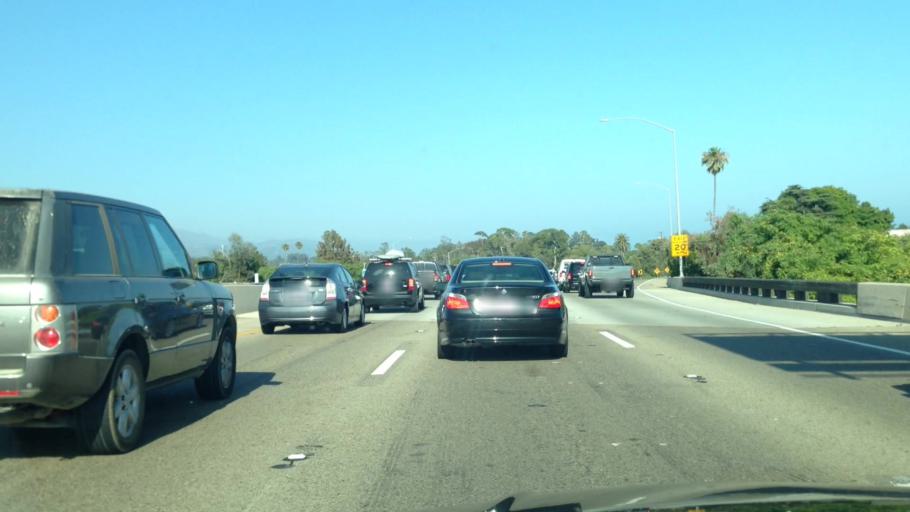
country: US
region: California
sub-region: Santa Barbara County
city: Santa Barbara
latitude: 34.4209
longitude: -119.6761
